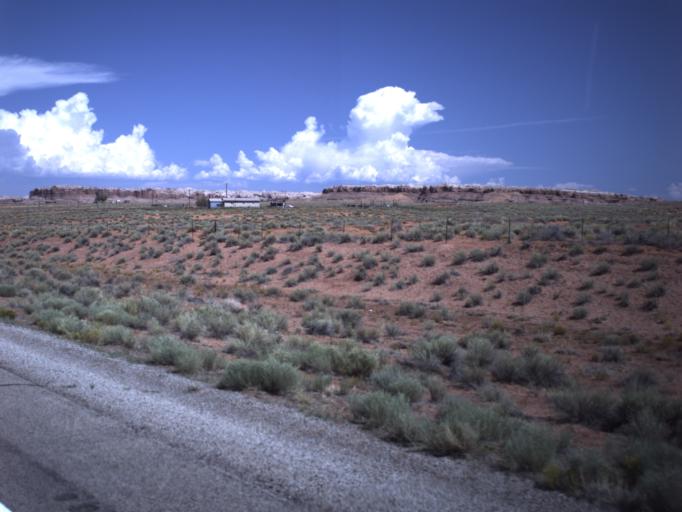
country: US
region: Utah
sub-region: San Juan County
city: Blanding
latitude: 37.1664
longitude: -109.5772
